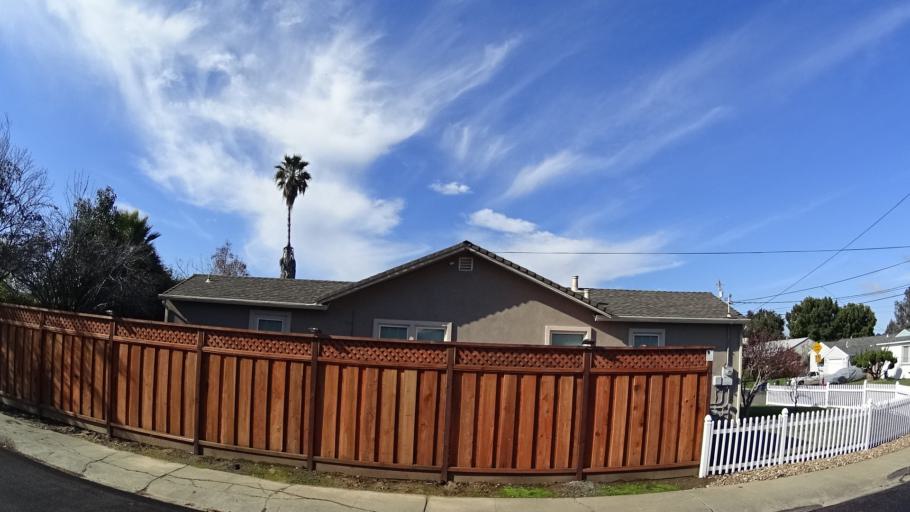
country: US
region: California
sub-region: Alameda County
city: Castro Valley
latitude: 37.6866
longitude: -122.0755
